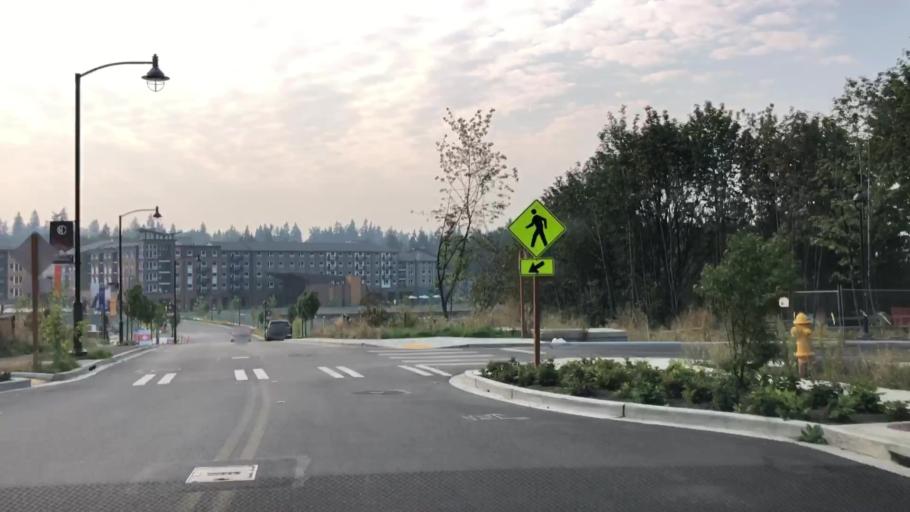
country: US
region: Washington
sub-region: King County
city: Newcastle
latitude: 47.5429
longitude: -122.1581
